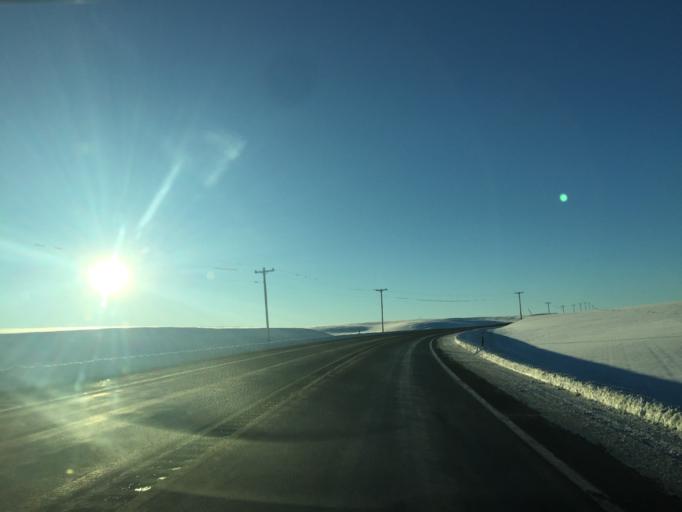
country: US
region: Washington
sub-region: Grant County
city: Soap Lake
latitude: 47.6001
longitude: -119.5168
